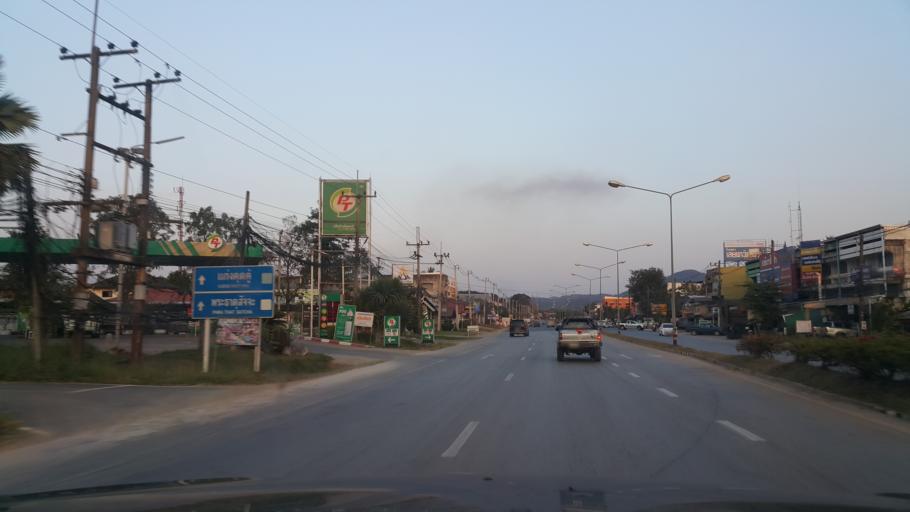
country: TH
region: Loei
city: Loei
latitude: 17.4946
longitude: 101.7142
